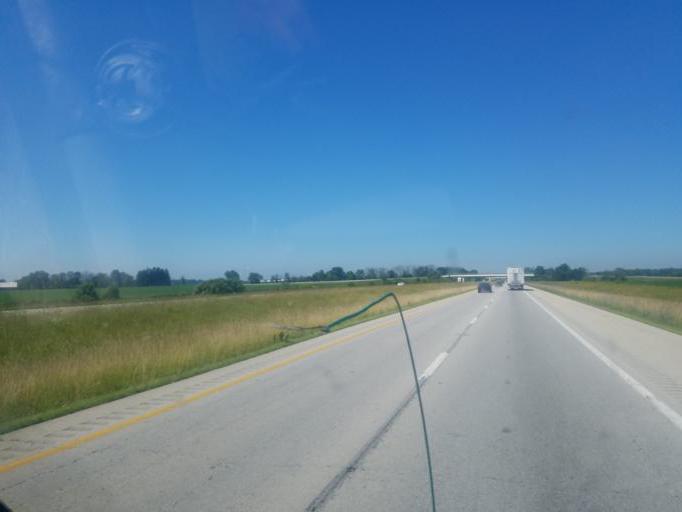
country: US
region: Ohio
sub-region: Clinton County
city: Wilmington
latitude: 39.5397
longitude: -83.7732
